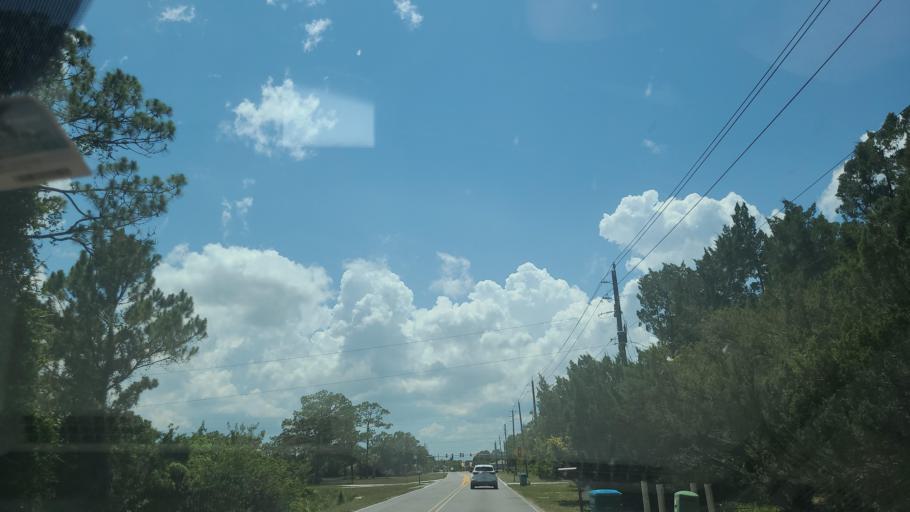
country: US
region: Florida
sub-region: Brevard County
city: Grant-Valkaria
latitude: 27.9536
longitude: -80.6196
